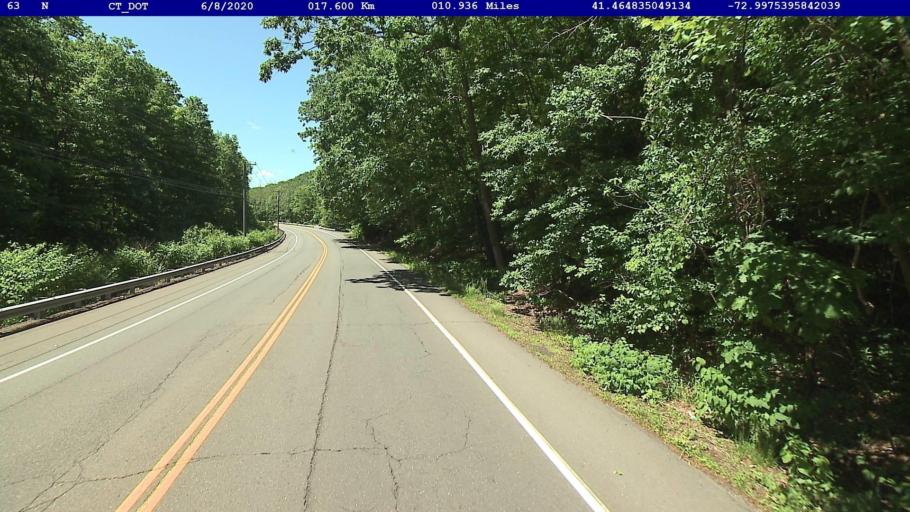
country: US
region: Connecticut
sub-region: New Haven County
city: Prospect
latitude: 41.4648
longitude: -72.9976
